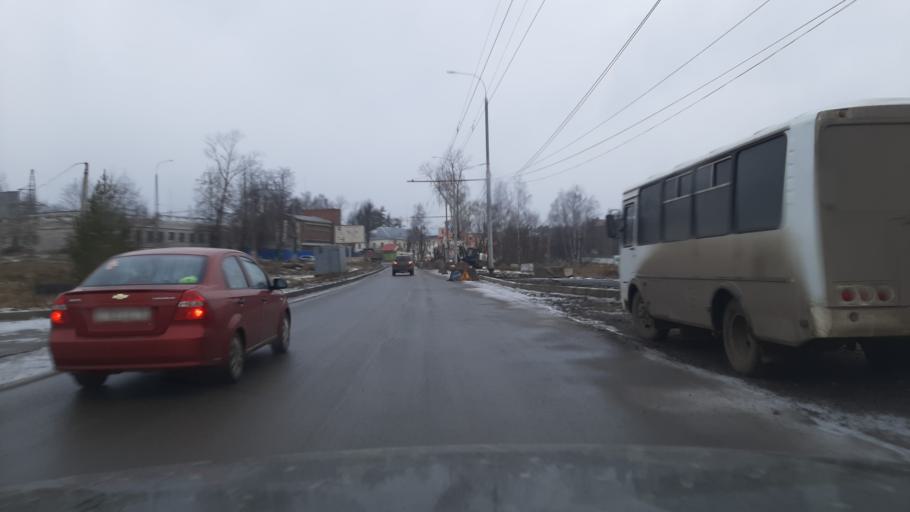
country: RU
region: Ivanovo
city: Kokhma
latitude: 56.9291
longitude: 41.0870
